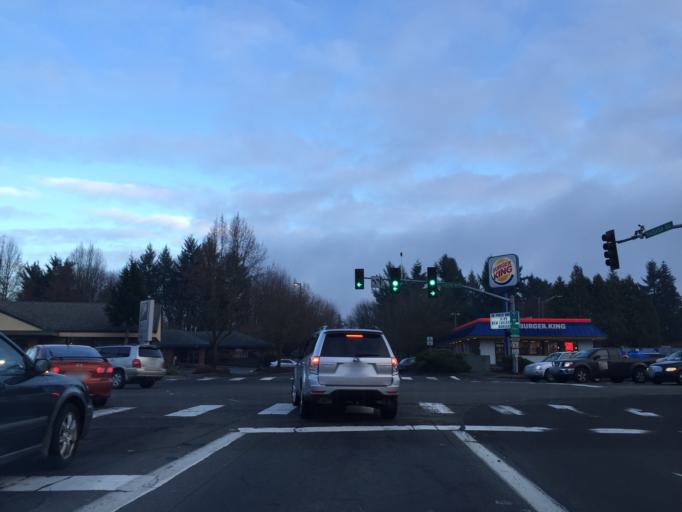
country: US
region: Washington
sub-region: Thurston County
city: Tumwater
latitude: 47.0000
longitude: -122.9092
